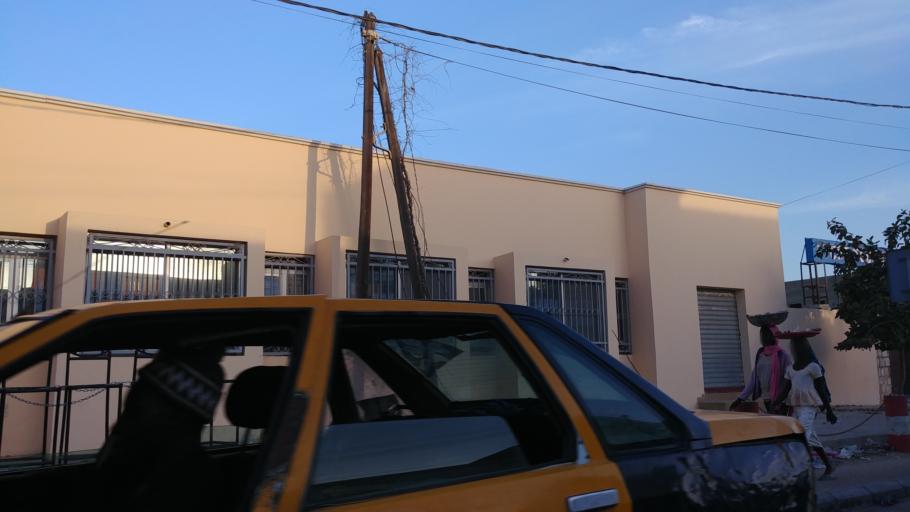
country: SN
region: Saint-Louis
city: Saint-Louis
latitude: 16.0193
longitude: -16.4908
